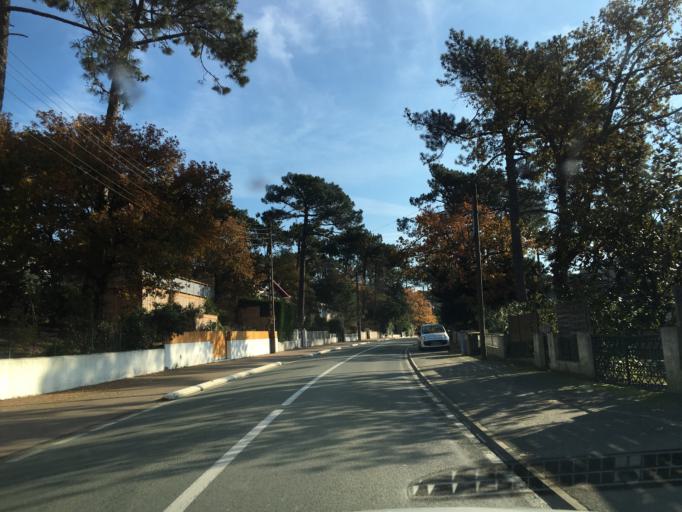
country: FR
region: Aquitaine
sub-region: Departement de la Gironde
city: Arcachon
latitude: 44.6438
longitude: -1.1752
